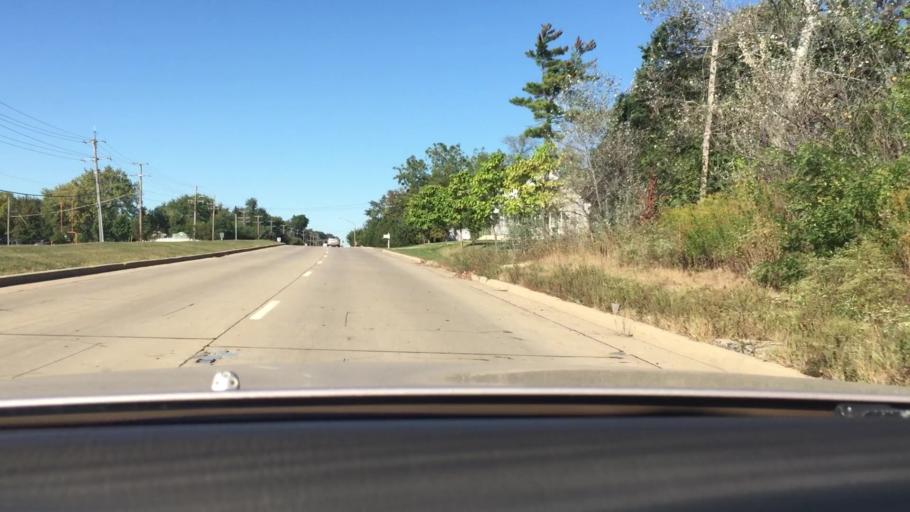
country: US
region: Illinois
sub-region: Lake County
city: Forest Lake
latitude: 42.1975
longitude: -88.0649
